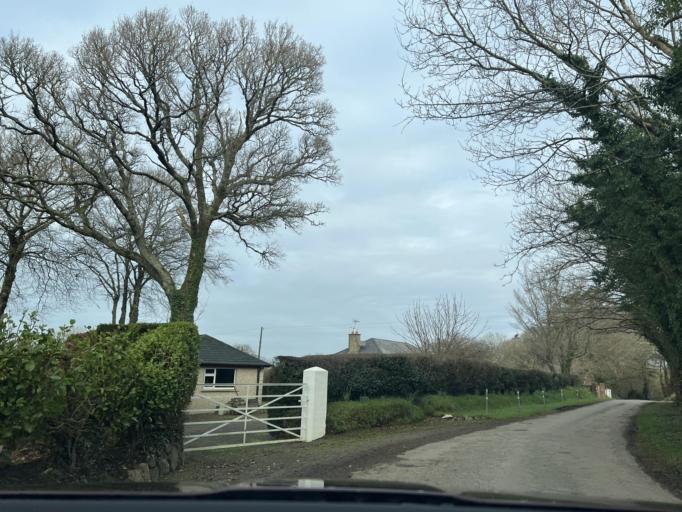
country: IE
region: Leinster
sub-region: Loch Garman
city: Loch Garman
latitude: 52.3654
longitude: -6.5322
